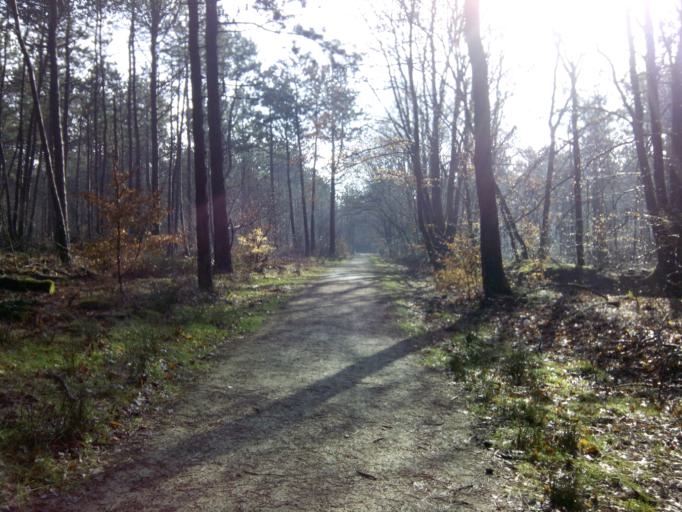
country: NL
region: Utrecht
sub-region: Gemeente Utrechtse Heuvelrug
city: Leersum
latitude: 52.0147
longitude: 5.4436
